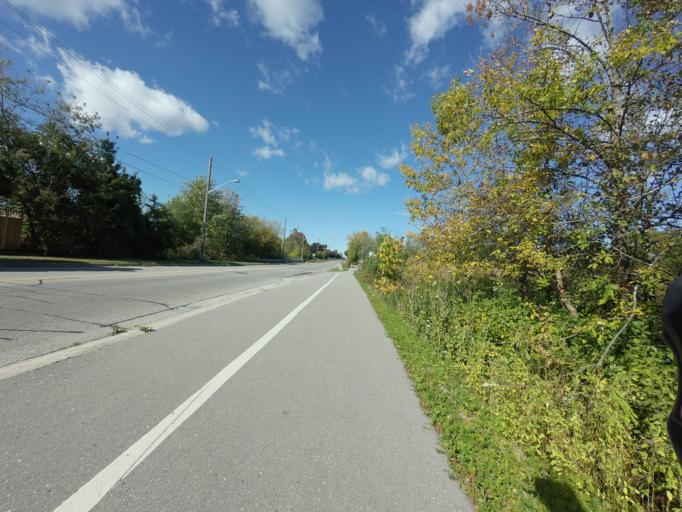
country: CA
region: Ontario
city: Ajax
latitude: 43.8311
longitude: -78.9911
